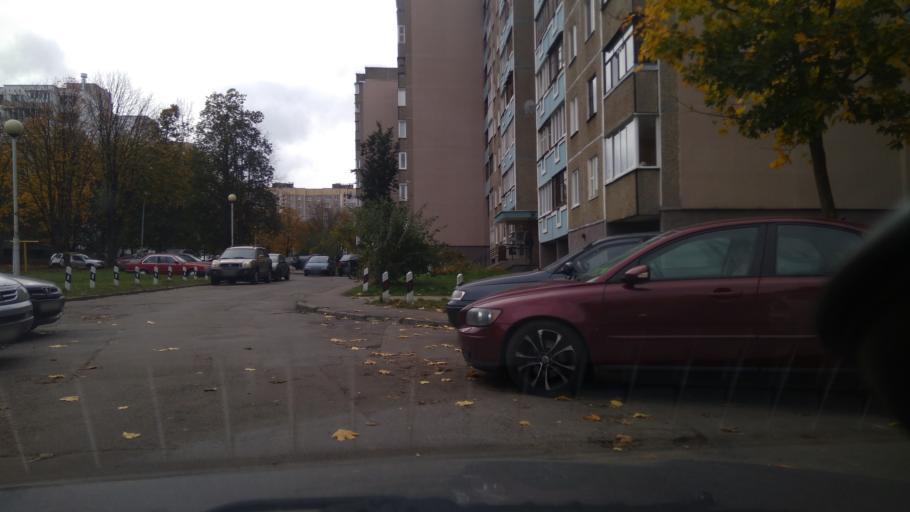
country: BY
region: Minsk
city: Novoye Medvezhino
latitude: 53.8966
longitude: 27.4826
